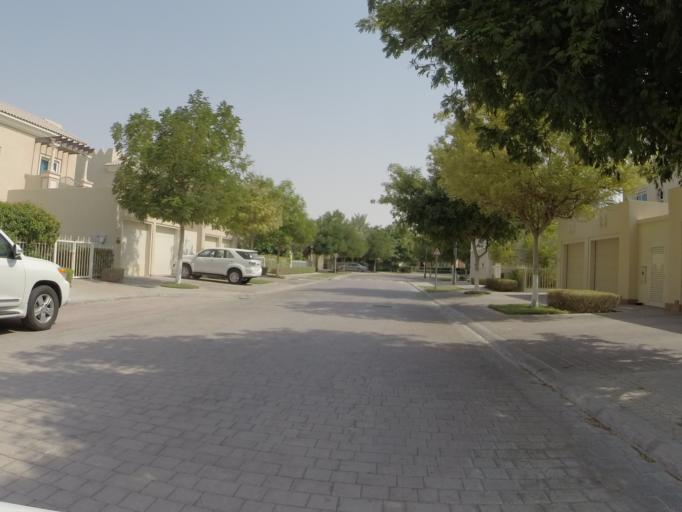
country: AE
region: Dubai
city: Dubai
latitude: 25.0332
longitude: 55.2153
